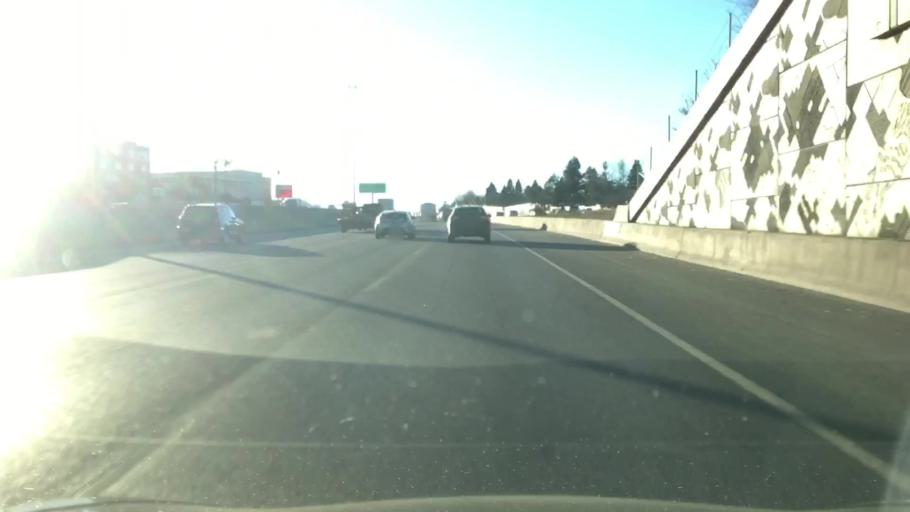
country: US
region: Colorado
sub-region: Arapahoe County
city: Cherry Hills Village
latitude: 39.6531
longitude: -104.9149
